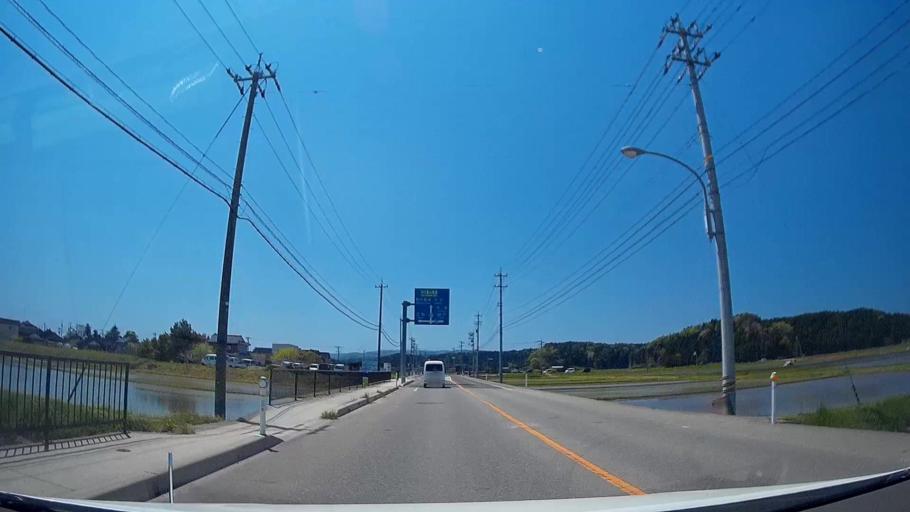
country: JP
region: Ishikawa
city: Nanao
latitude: 37.4502
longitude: 137.2914
